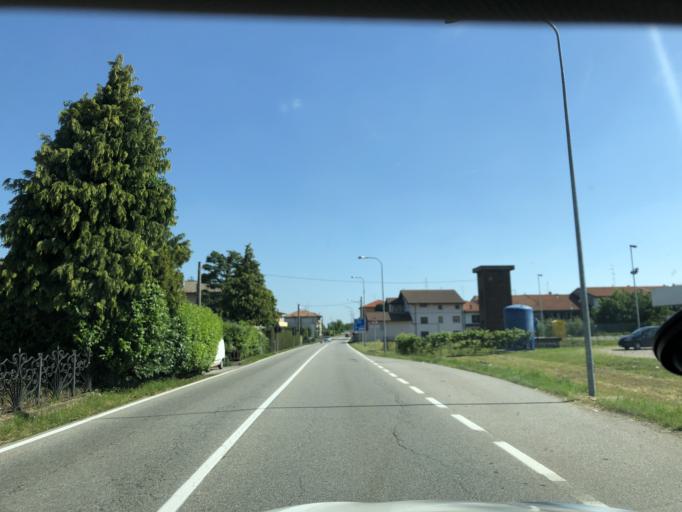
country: IT
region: Piedmont
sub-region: Provincia di Novara
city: Oleggio
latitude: 45.5979
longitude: 8.6448
